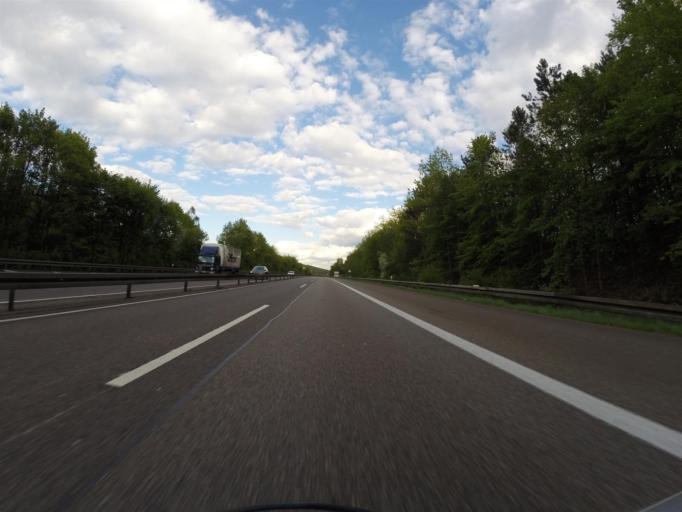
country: DE
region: Saarland
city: Bous
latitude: 49.2673
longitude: 6.8140
